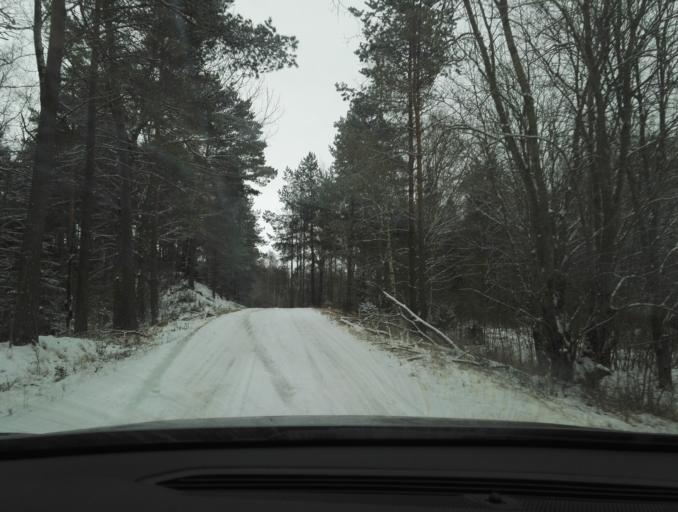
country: SE
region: Kronoberg
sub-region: Vaxjo Kommun
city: Vaexjoe
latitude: 56.8538
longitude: 14.7611
